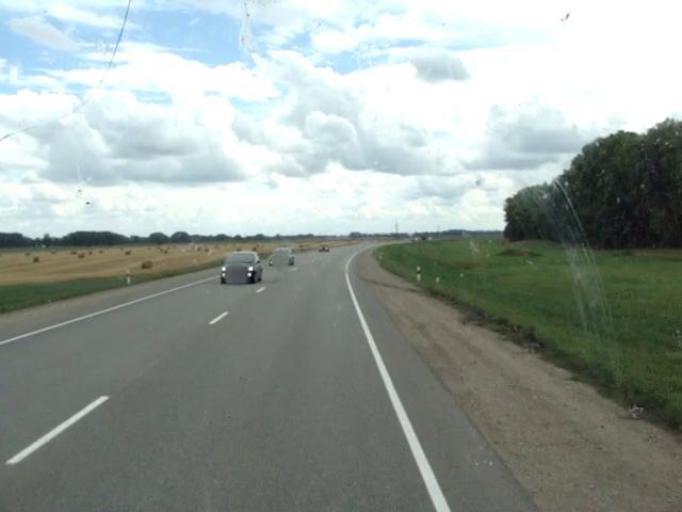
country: RU
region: Altai Krai
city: Shubenka
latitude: 52.6837
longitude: 85.0444
